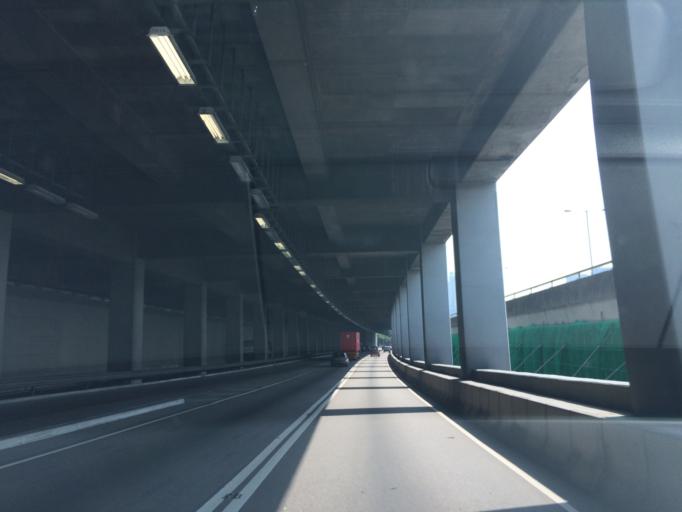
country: HK
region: Sham Shui Po
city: Sham Shui Po
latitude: 22.3273
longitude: 114.1529
